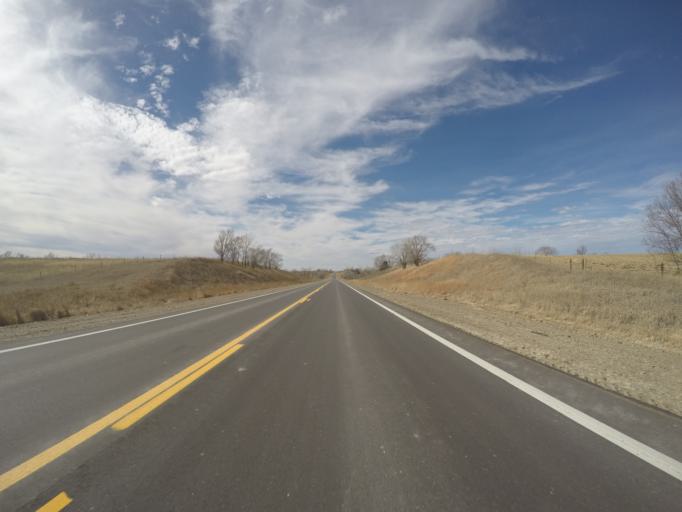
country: US
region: Nebraska
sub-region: Franklin County
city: Franklin
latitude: 40.0962
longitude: -98.9132
